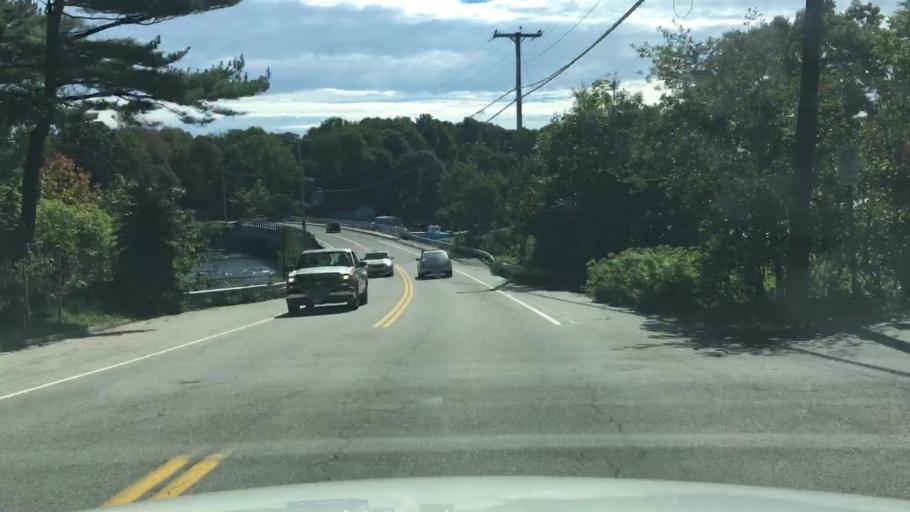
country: US
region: Maine
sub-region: York County
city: Kittery Point
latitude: 43.0840
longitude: -70.7201
